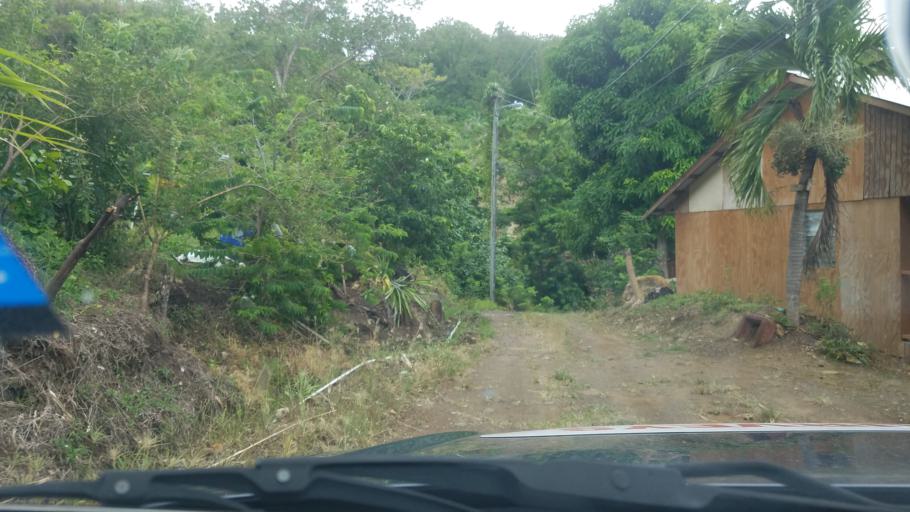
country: LC
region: Castries Quarter
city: Bisee
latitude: 14.0129
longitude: -60.9268
